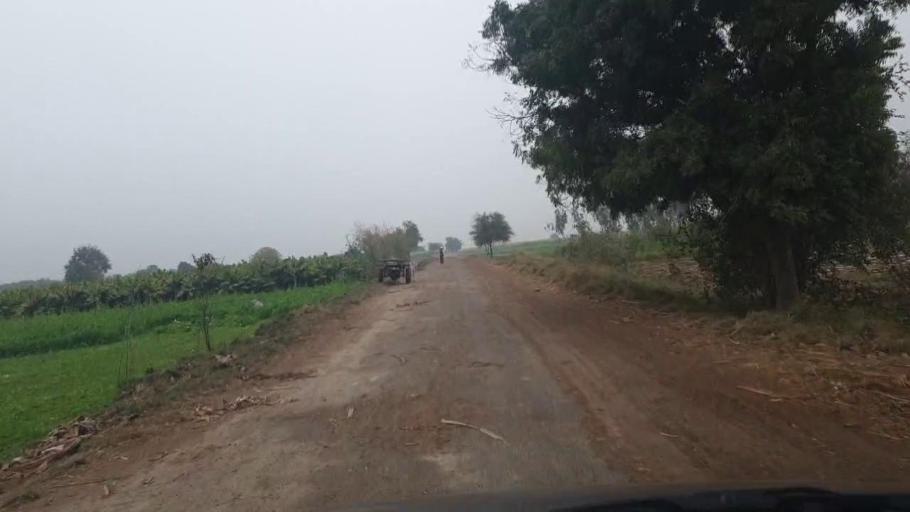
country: PK
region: Sindh
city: Tando Adam
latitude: 25.8028
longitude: 68.6769
